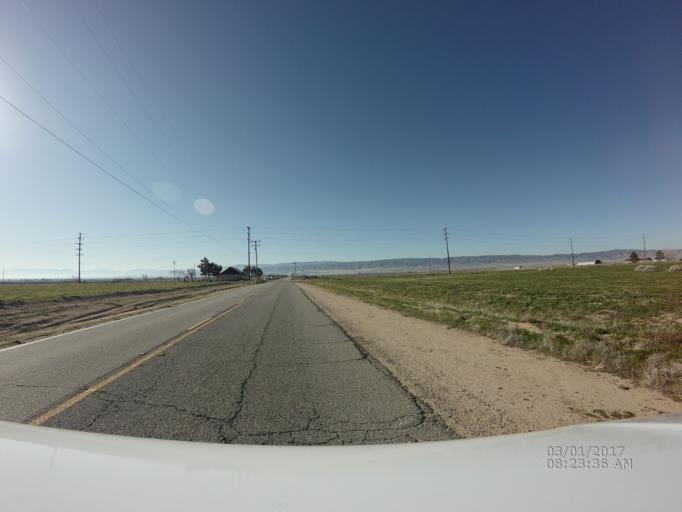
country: US
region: California
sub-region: Los Angeles County
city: Quartz Hill
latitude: 34.7195
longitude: -118.2546
